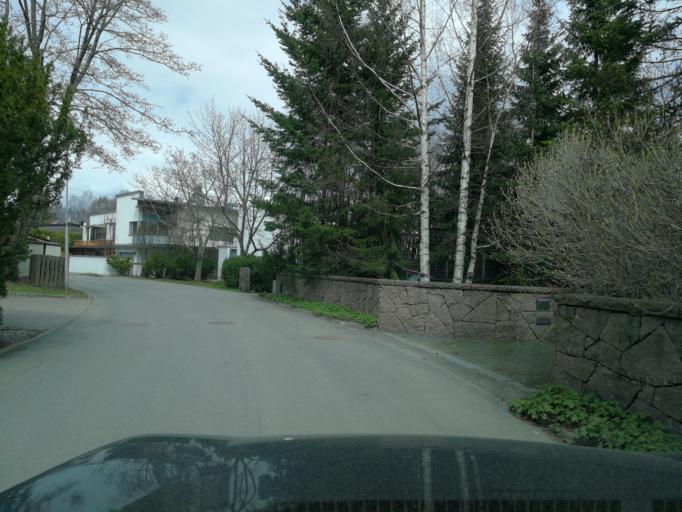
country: FI
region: Uusimaa
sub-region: Helsinki
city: Otaniemi
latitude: 60.1636
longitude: 24.8065
